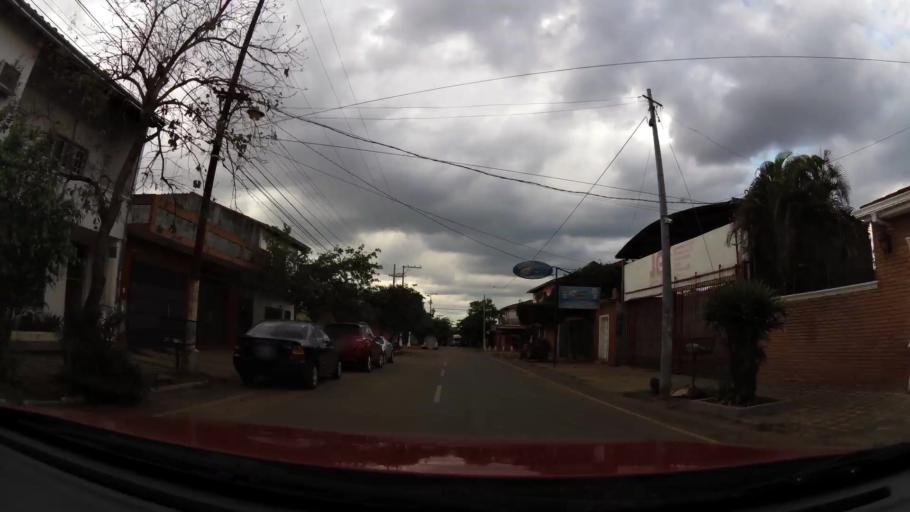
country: PY
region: Central
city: Fernando de la Mora
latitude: -25.3290
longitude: -57.5540
